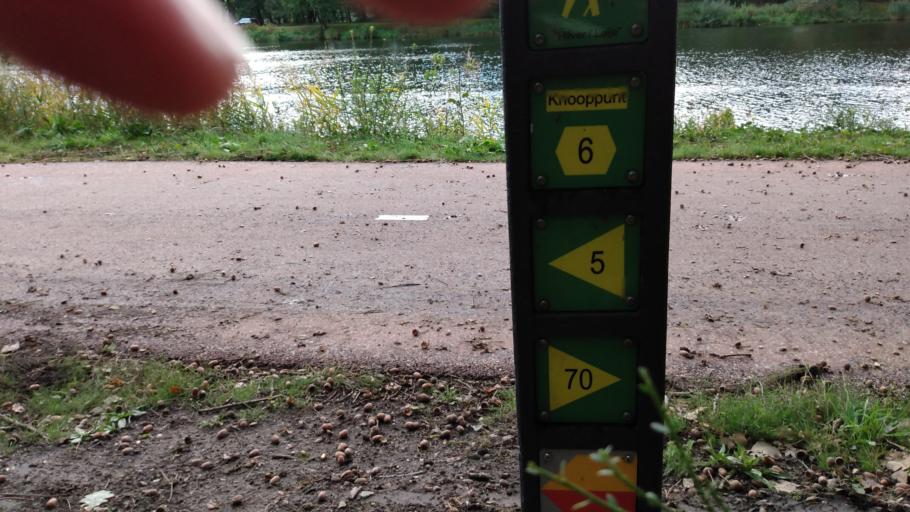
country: NL
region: North Brabant
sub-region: Gemeente Hilvarenbeek
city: Hilvarenbeek
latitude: 51.5304
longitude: 5.1303
